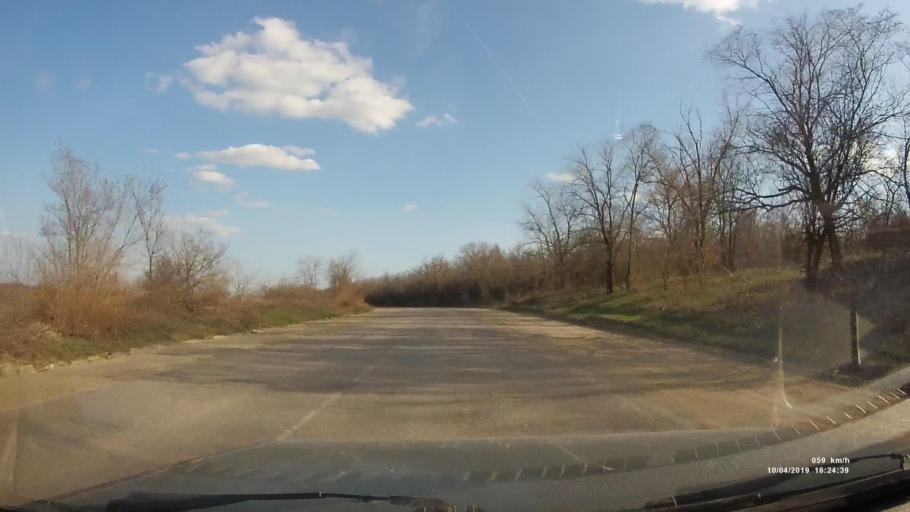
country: RU
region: Rostov
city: Staraya Stanitsa
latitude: 48.2979
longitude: 40.3161
